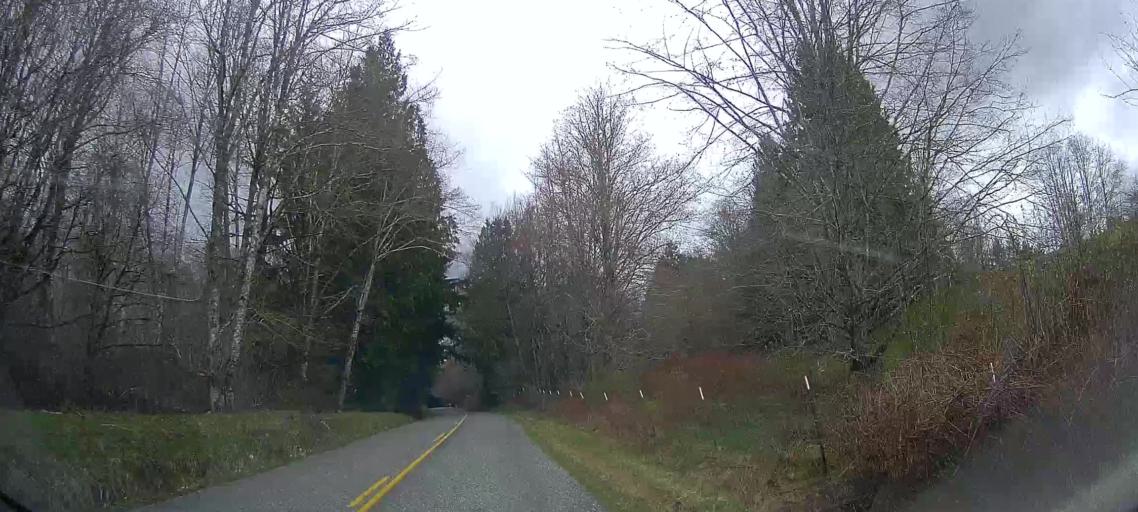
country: US
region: Washington
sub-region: Skagit County
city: Burlington
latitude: 48.5787
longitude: -122.3376
